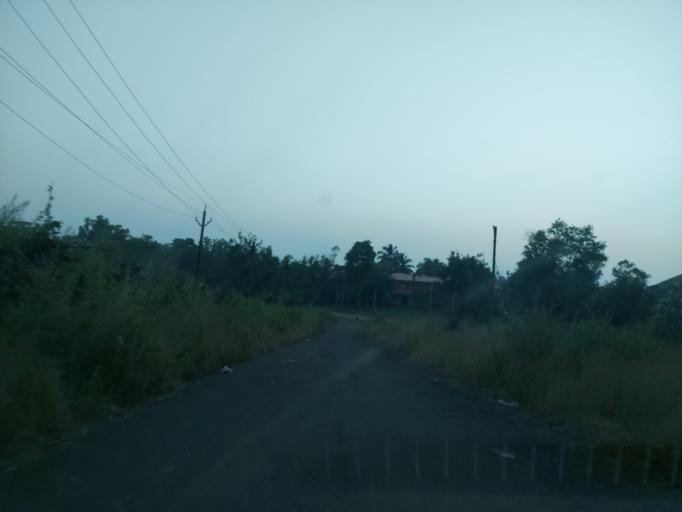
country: IN
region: Maharashtra
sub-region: Sindhudurg
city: Kudal
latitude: 16.1135
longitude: 73.6992
